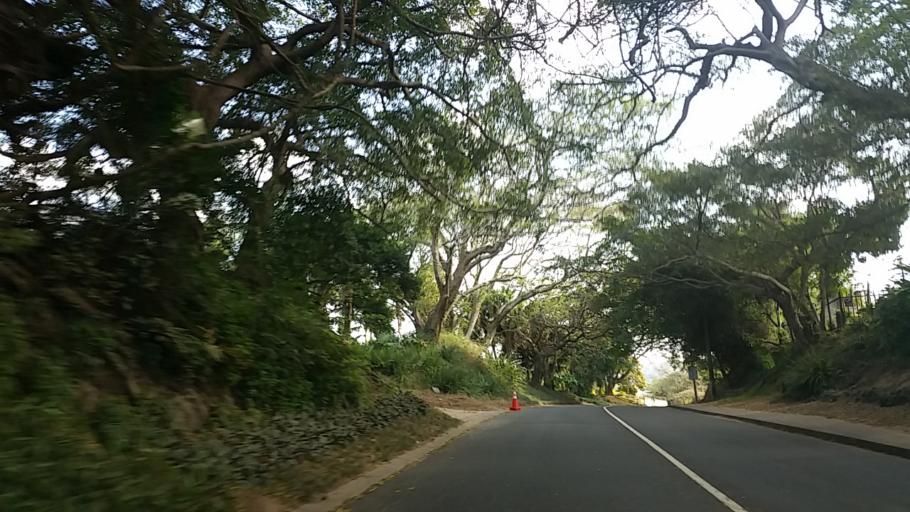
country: ZA
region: KwaZulu-Natal
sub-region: eThekwini Metropolitan Municipality
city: Berea
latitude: -29.8294
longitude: 30.9346
